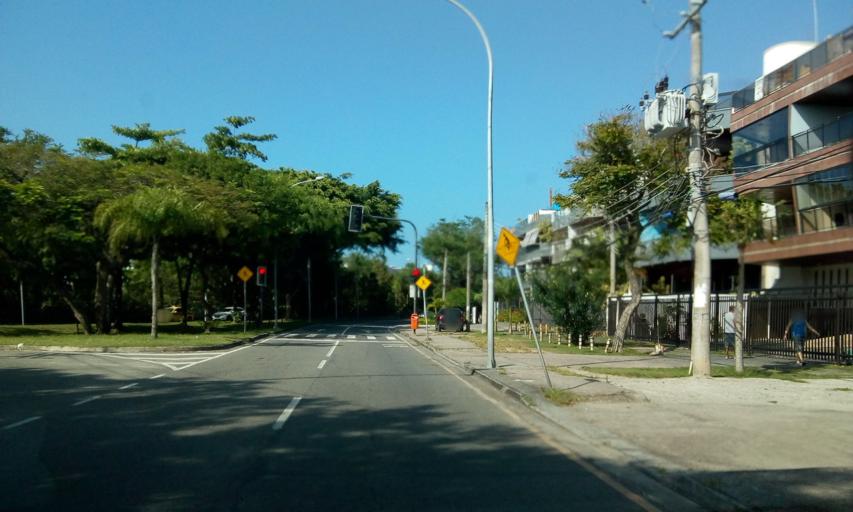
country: BR
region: Rio de Janeiro
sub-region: Nilopolis
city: Nilopolis
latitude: -23.0208
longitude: -43.4542
